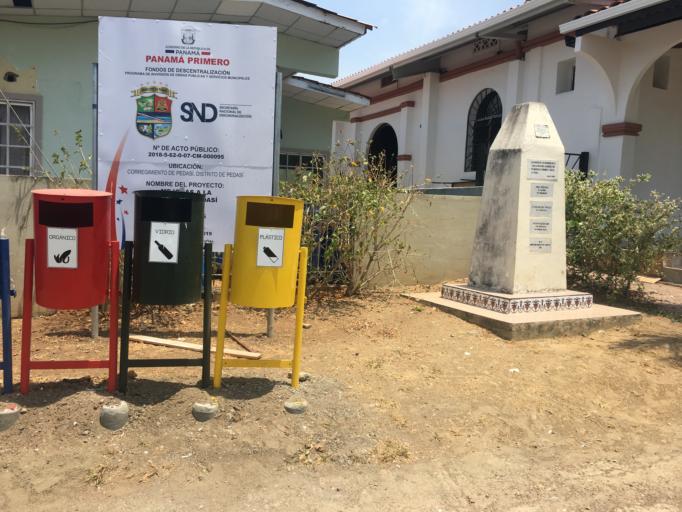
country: PA
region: Los Santos
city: Pedasi
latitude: 7.5293
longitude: -80.0262
